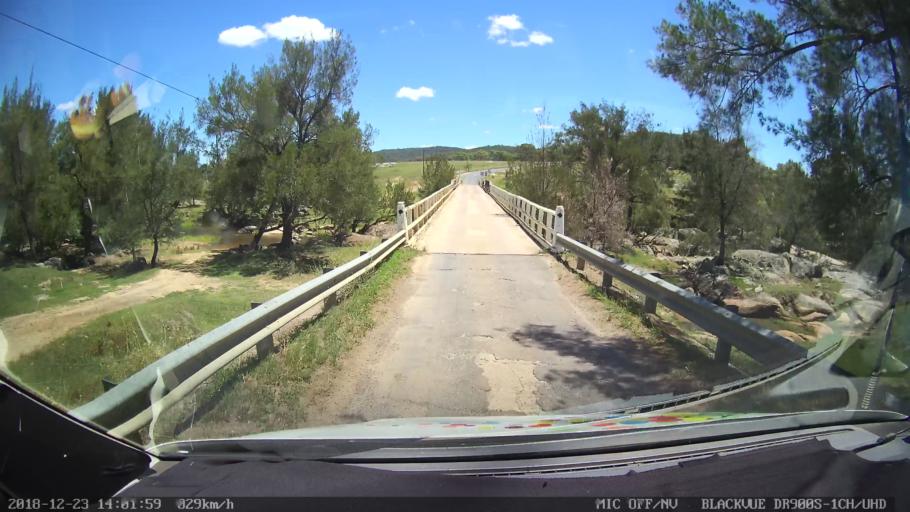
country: AU
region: New South Wales
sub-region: Tamworth Municipality
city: Manilla
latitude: -30.6227
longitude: 151.1099
